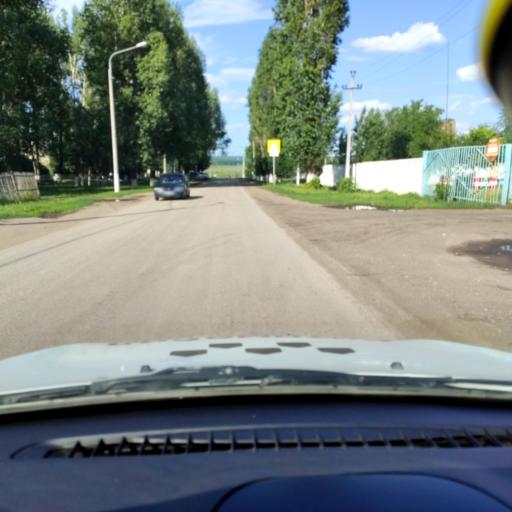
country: RU
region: Samara
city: Tol'yatti
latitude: 53.3521
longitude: 49.2988
